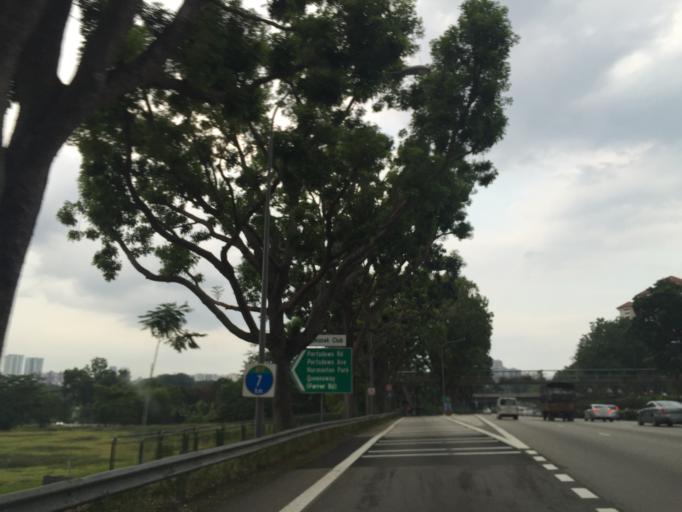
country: SG
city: Singapore
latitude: 1.2909
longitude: 103.7907
